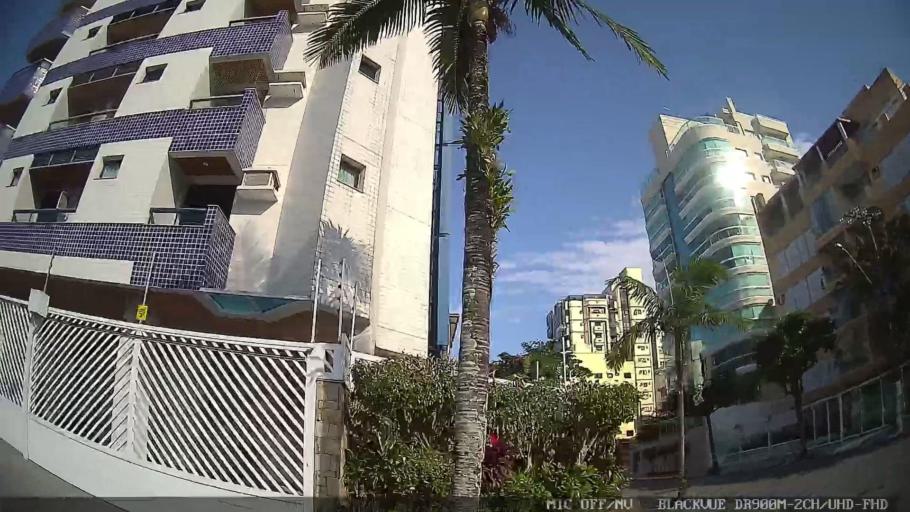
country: BR
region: Sao Paulo
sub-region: Guaruja
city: Guaruja
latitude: -23.9840
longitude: -46.2213
